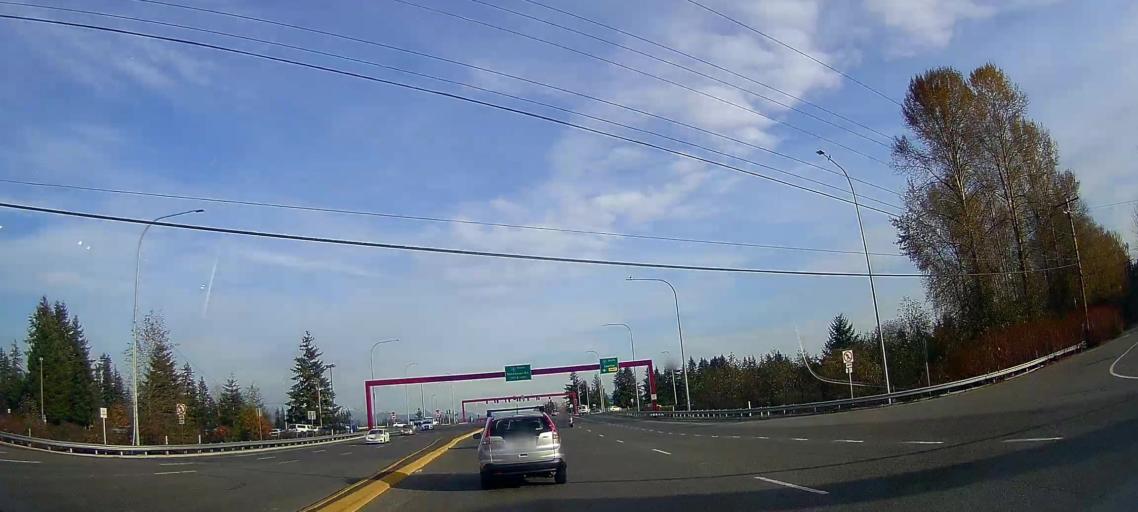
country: US
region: Washington
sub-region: Snohomish County
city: Marysville
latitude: 48.1003
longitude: -122.1880
